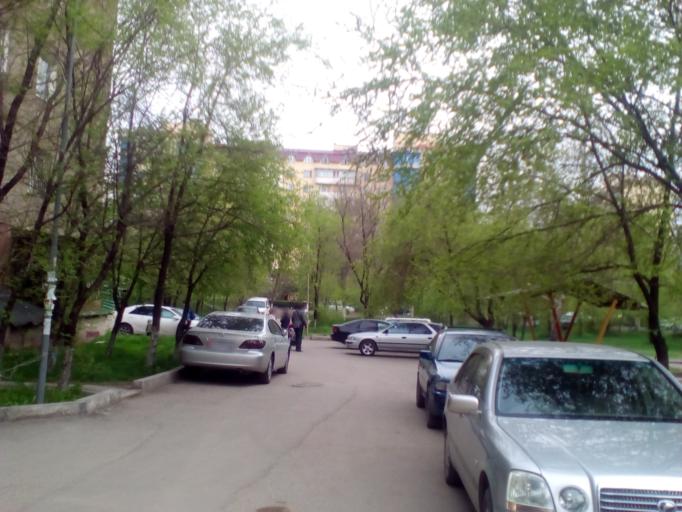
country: KZ
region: Almaty Qalasy
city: Almaty
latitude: 43.2394
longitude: 76.8260
